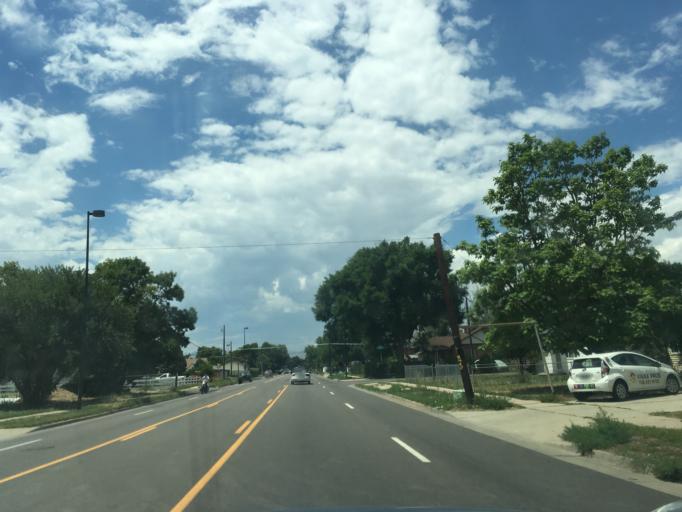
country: US
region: Colorado
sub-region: Arapahoe County
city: Sheridan
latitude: 39.6968
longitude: -105.0195
